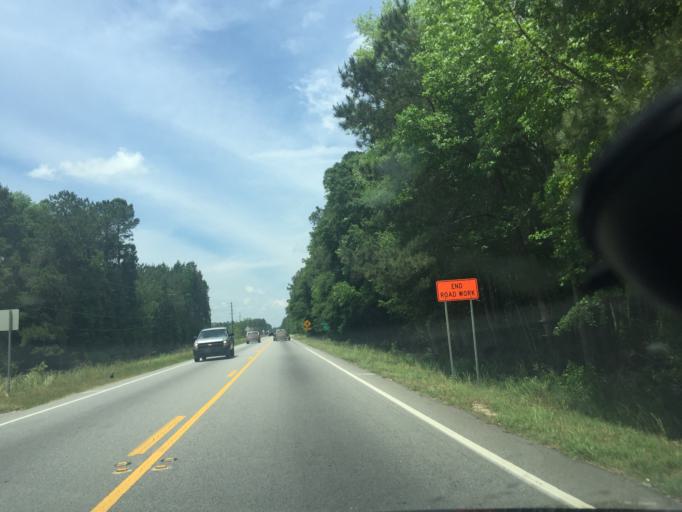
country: US
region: Georgia
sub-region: Chatham County
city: Bloomingdale
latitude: 32.1590
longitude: -81.3664
